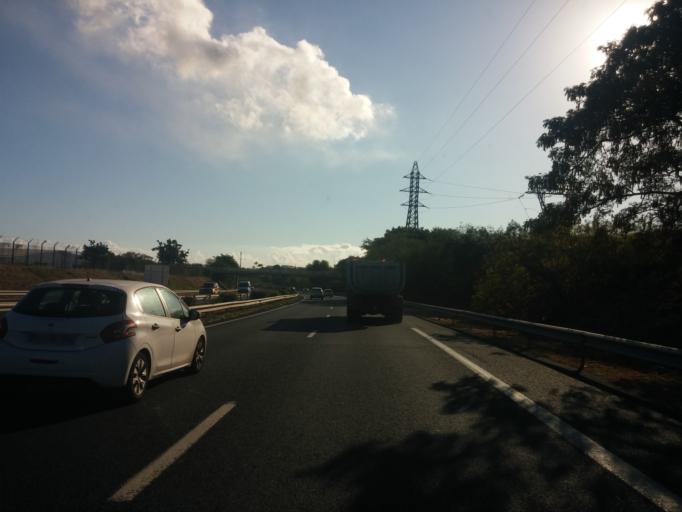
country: RE
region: Reunion
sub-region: Reunion
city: La Possession
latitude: -20.9418
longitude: 55.3287
